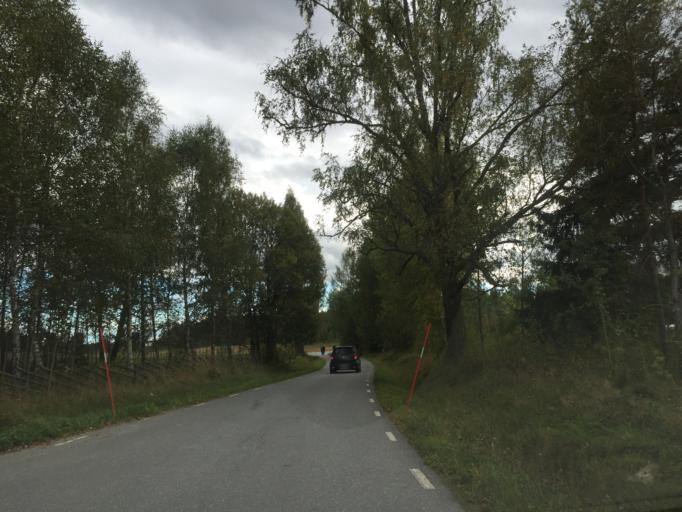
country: SE
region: OErebro
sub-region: Orebro Kommun
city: Hovsta
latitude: 59.3701
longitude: 15.1723
